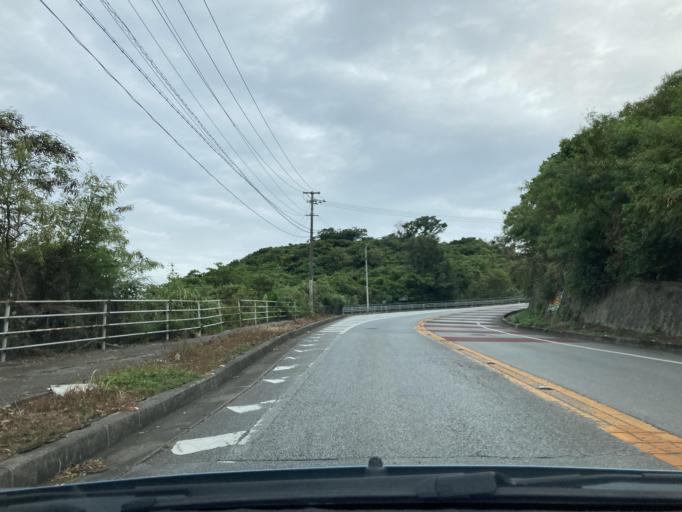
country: JP
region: Okinawa
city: Tomigusuku
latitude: 26.1648
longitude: 127.7727
